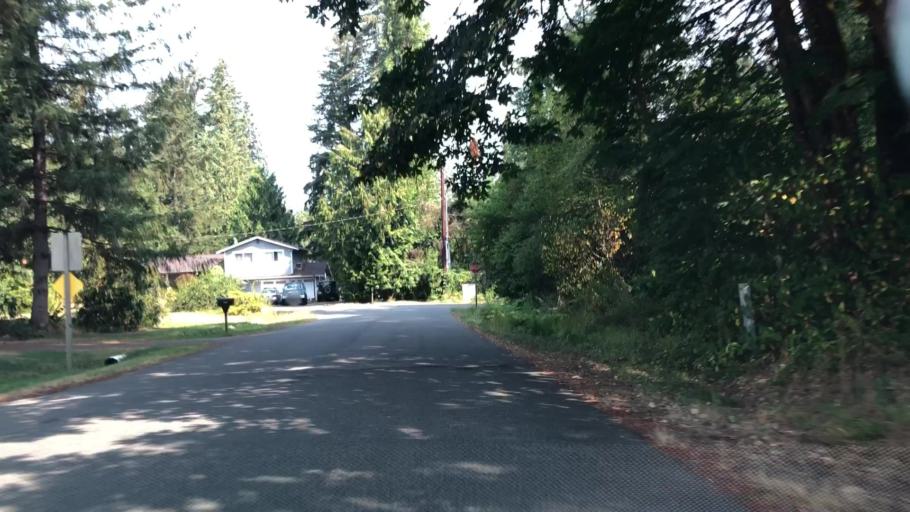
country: US
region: Washington
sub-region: King County
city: Cottage Lake
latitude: 47.7422
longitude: -122.0875
